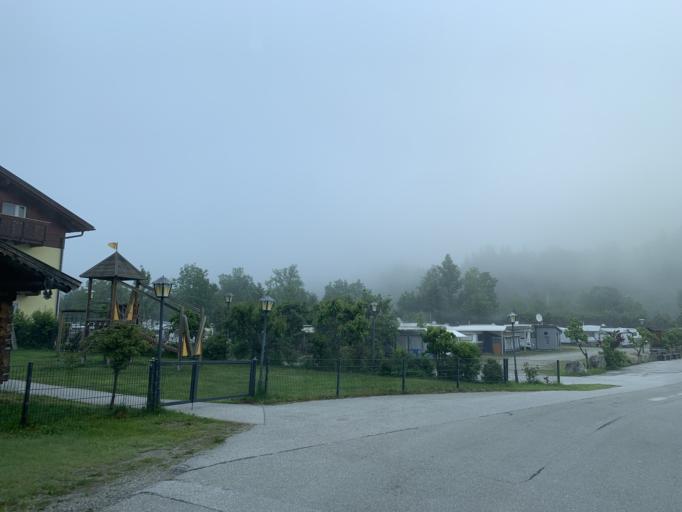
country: AT
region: Salzburg
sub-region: Politischer Bezirk Sankt Johann im Pongau
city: Forstau
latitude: 47.3891
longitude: 13.5958
